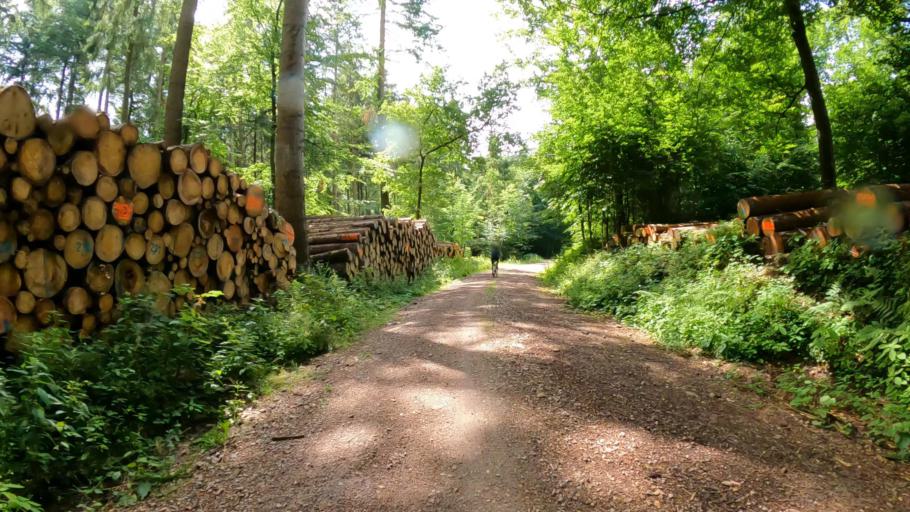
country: DE
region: Lower Saxony
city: Neu Wulmstorf
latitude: 53.4104
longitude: 9.8618
